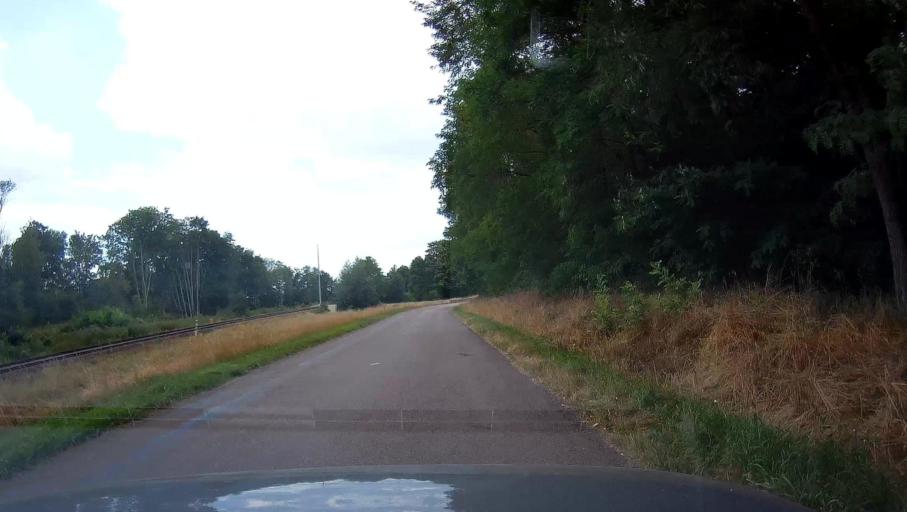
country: FR
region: Champagne-Ardenne
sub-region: Departement de la Haute-Marne
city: Langres
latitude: 47.8596
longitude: 5.3706
